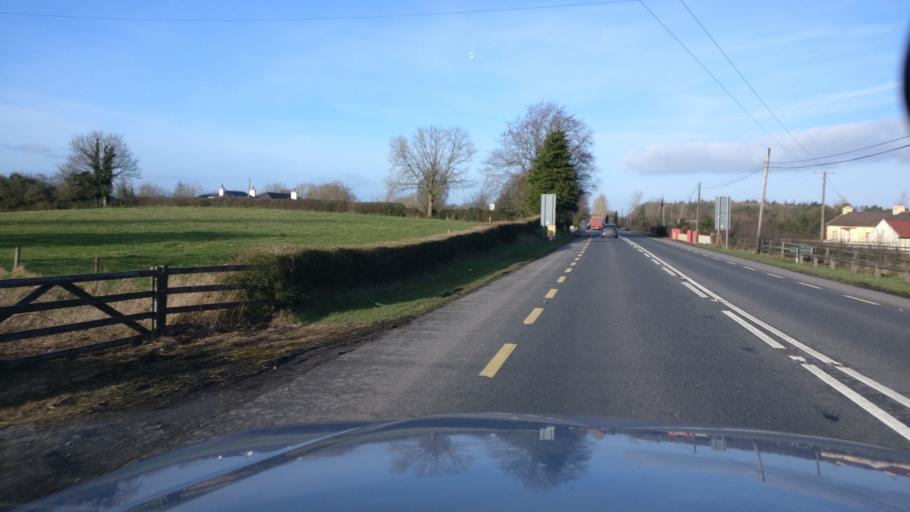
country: IE
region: Leinster
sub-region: Uibh Fhaili
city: Tullamore
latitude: 53.2229
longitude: -7.4759
